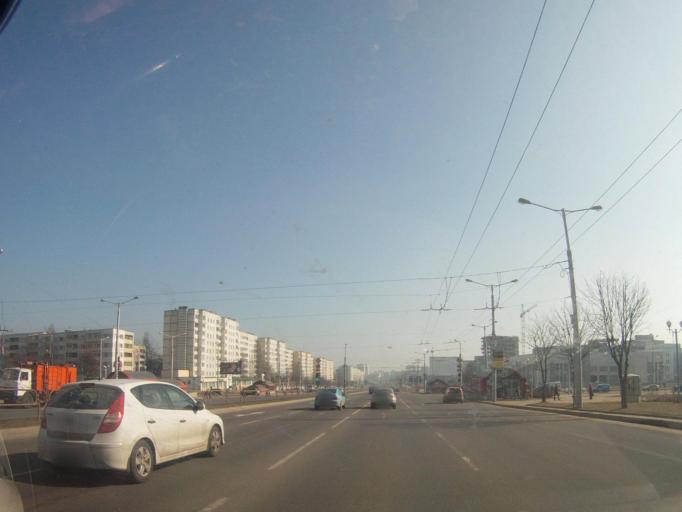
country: BY
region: Minsk
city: Novoye Medvezhino
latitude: 53.9082
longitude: 27.4799
